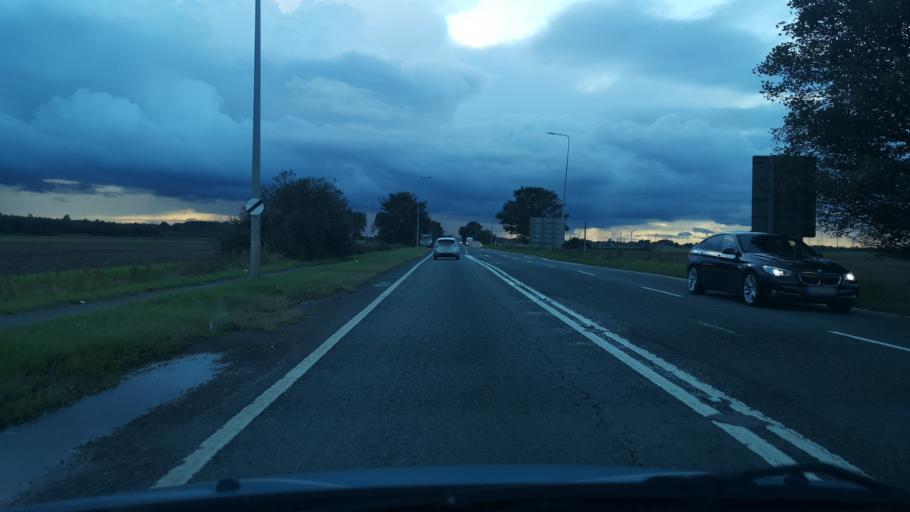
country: GB
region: England
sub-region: North Lincolnshire
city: Gunness
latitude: 53.5895
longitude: -0.7027
